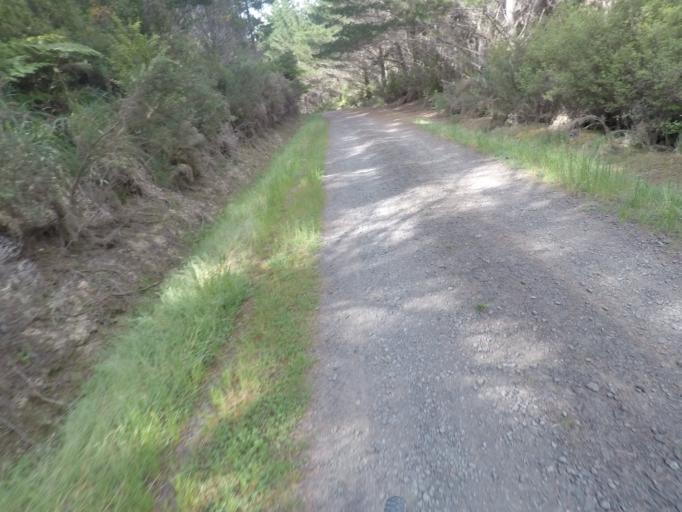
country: NZ
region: Auckland
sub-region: Auckland
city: Muriwai Beach
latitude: -36.7416
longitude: 174.5716
